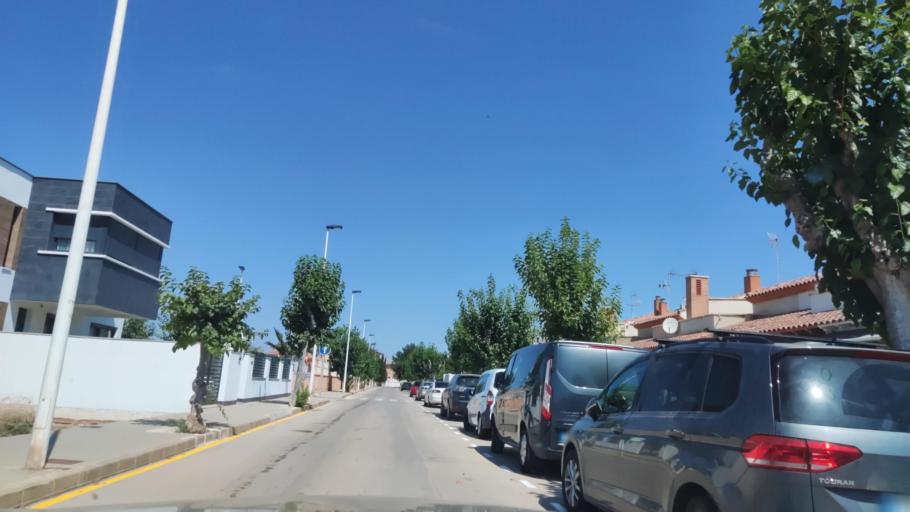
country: ES
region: Murcia
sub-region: Murcia
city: Los Alcazares
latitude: 37.7517
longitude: -0.8502
